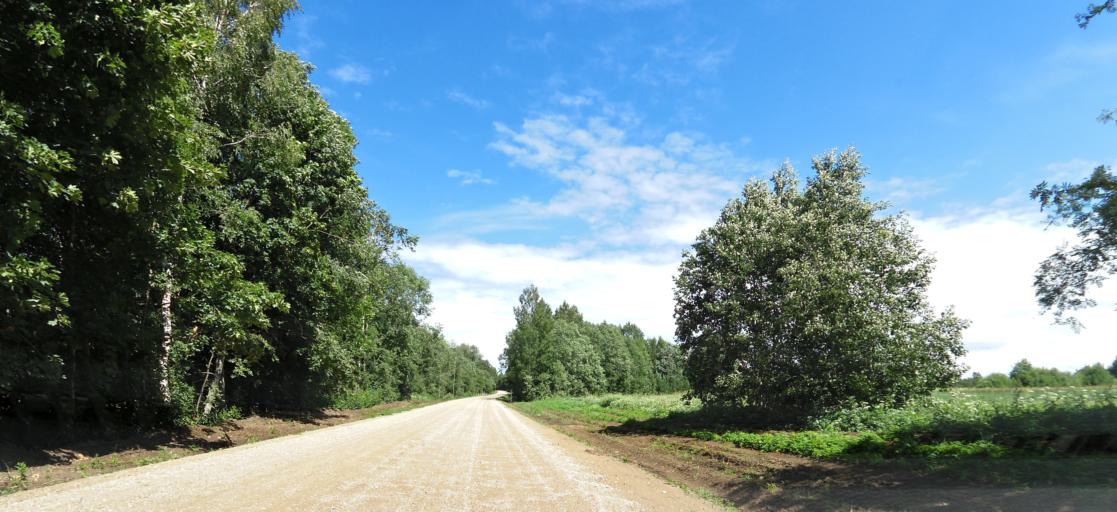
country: LT
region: Panevezys
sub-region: Birzai
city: Birzai
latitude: 56.4068
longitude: 24.7933
